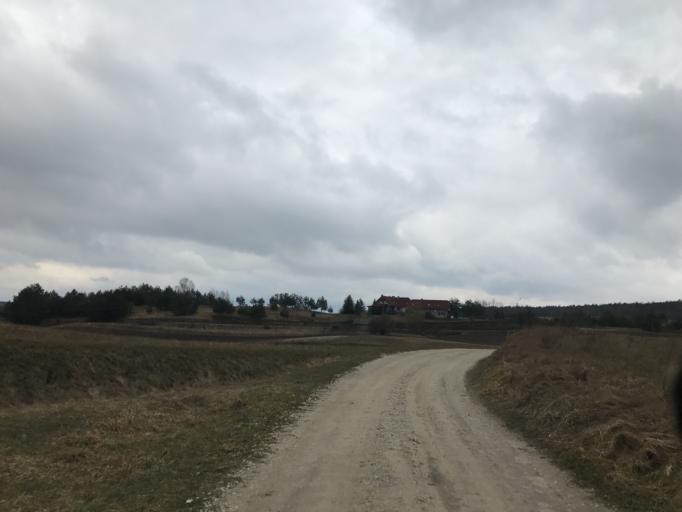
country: PL
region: Kujawsko-Pomorskie
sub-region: Powiat brodnicki
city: Gorzno
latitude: 53.2059
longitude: 19.6724
